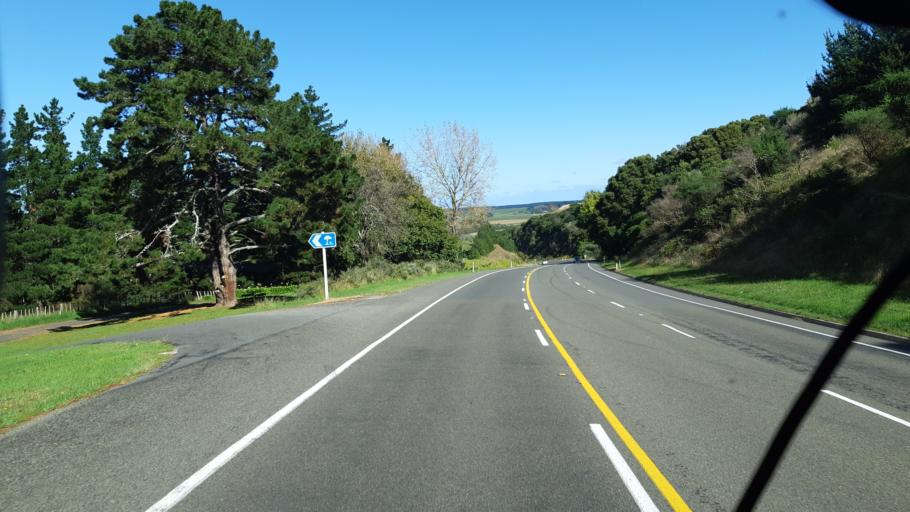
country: NZ
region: Manawatu-Wanganui
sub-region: Wanganui District
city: Wanganui
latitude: -39.9976
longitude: 175.1689
